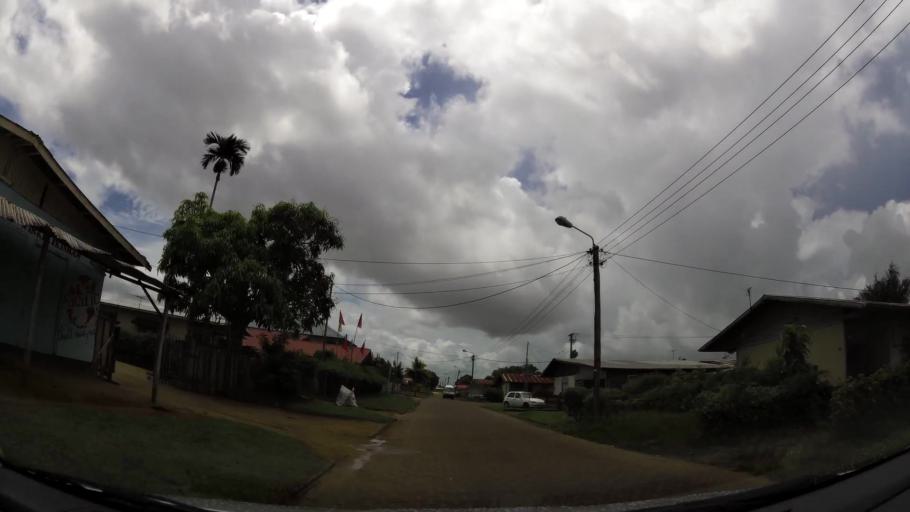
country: SR
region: Paramaribo
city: Paramaribo
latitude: 5.8285
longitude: -55.2260
